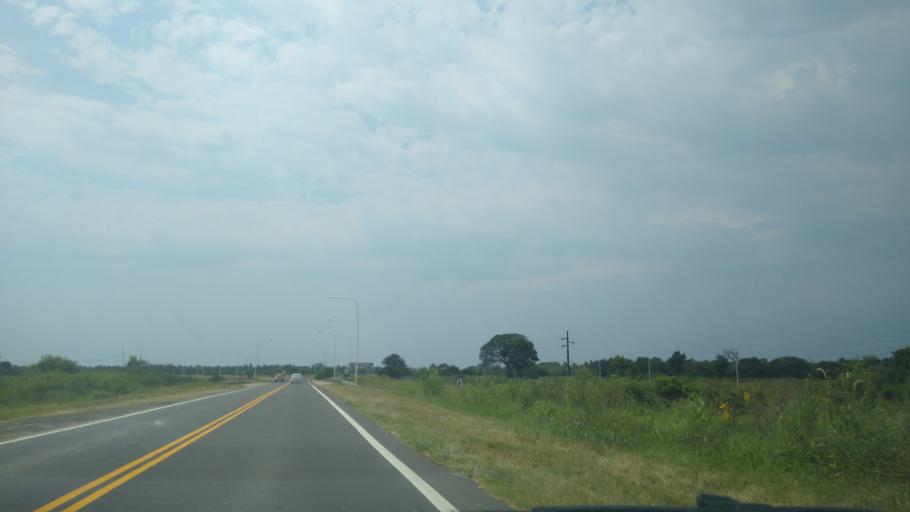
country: AR
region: Chaco
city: Margarita Belen
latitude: -27.0915
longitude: -58.9592
